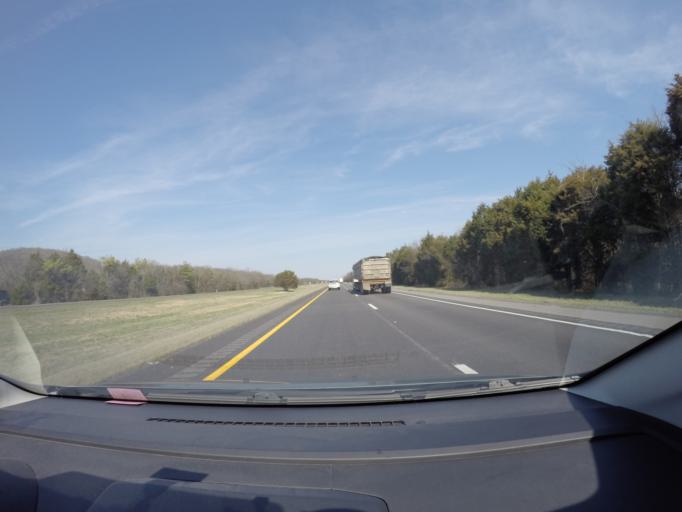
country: US
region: Tennessee
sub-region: Rutherford County
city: Plainview
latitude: 35.6721
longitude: -86.2814
